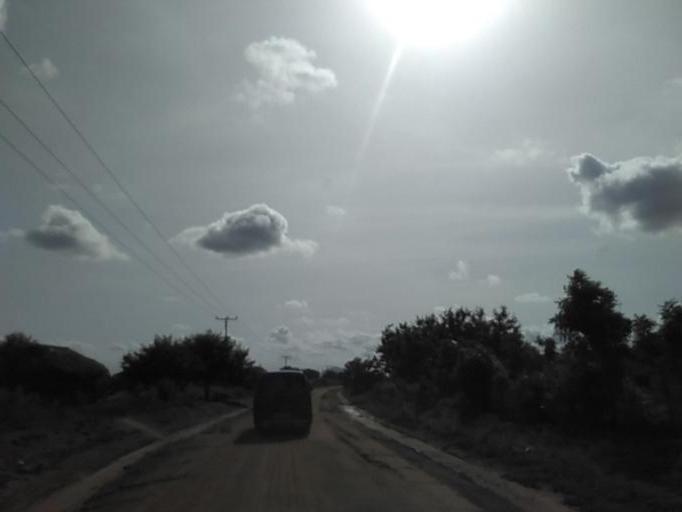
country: GH
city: Akropong
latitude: 6.0319
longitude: 0.3382
